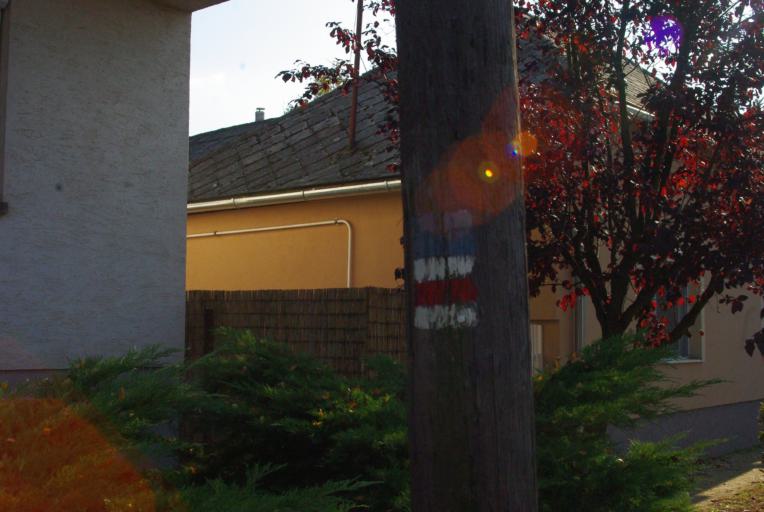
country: HU
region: Komarom-Esztergom
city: Piliscsev
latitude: 47.6757
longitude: 18.8197
